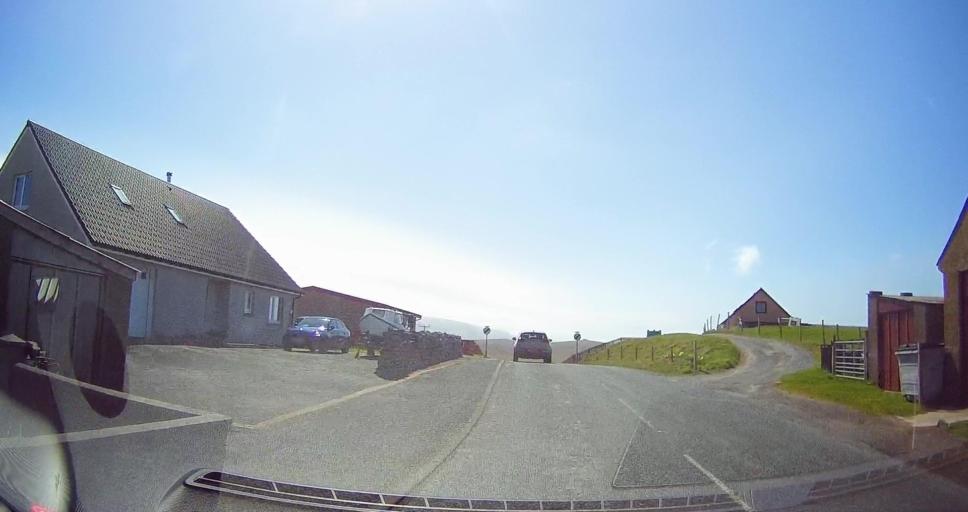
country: GB
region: Scotland
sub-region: Shetland Islands
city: Sandwick
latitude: 60.0967
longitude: -1.3219
